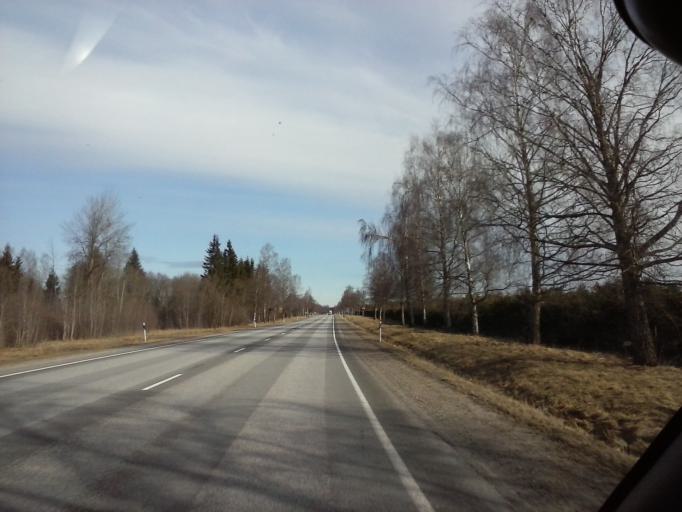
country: EE
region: Jaervamaa
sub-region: Paide linn
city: Paide
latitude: 58.9894
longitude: 25.5918
